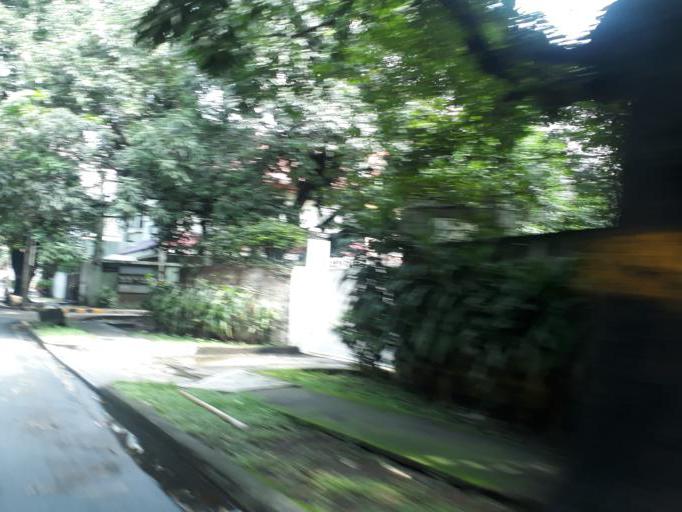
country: PH
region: Metro Manila
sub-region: San Juan
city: San Juan
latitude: 14.6194
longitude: 121.0284
